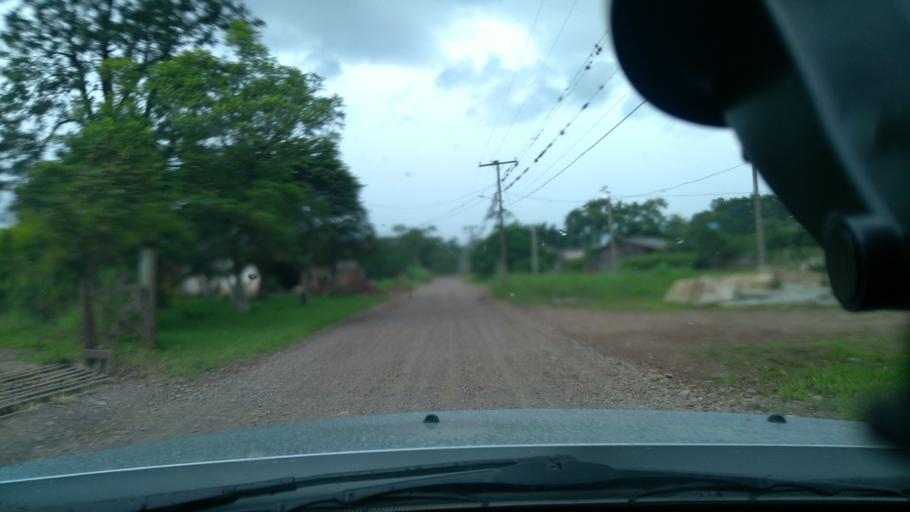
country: BR
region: Rio Grande do Sul
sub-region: Torres
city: Torres
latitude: -29.2053
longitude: -49.9727
